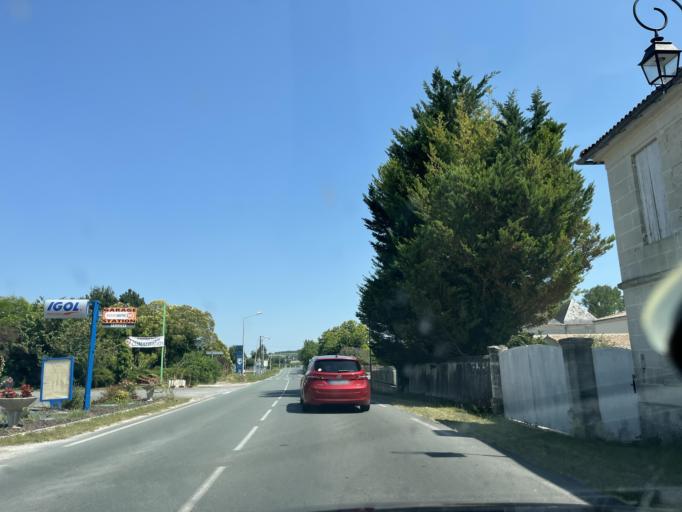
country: FR
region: Poitou-Charentes
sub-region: Departement de la Charente-Maritime
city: Mirambeau
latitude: 45.4218
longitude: -0.6381
